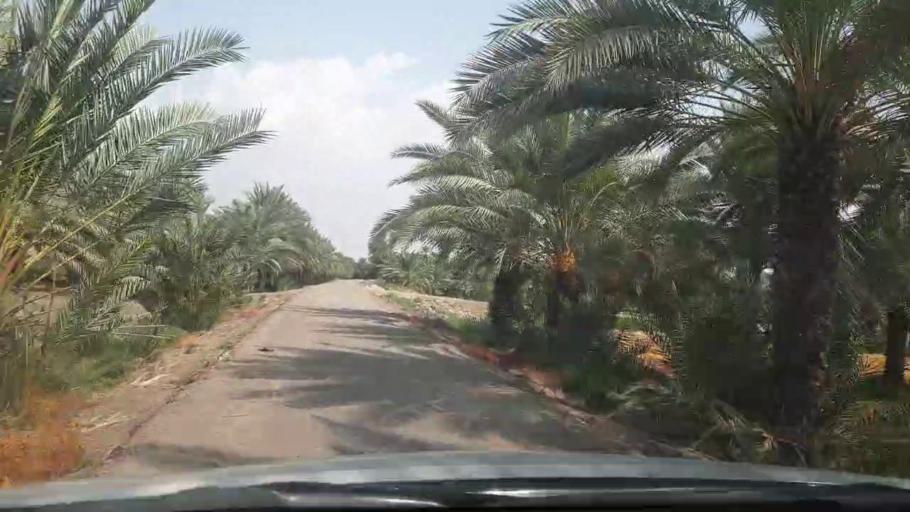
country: PK
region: Sindh
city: Khairpur
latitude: 27.5543
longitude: 68.8435
